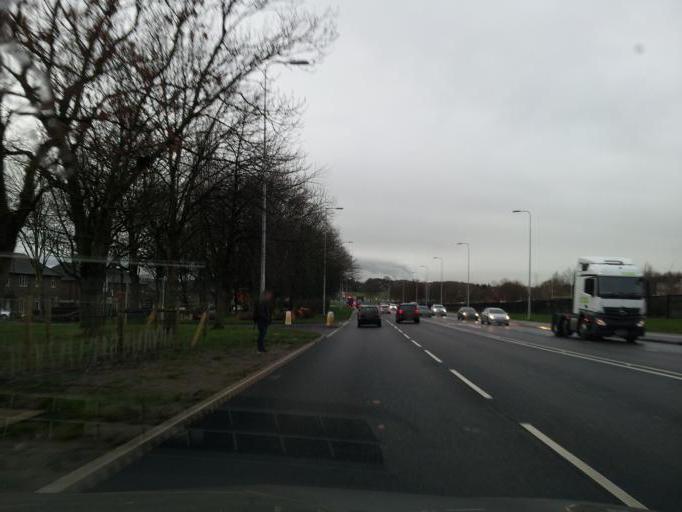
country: GB
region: England
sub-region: Nottinghamshire
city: Ruddington
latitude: 52.9105
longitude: -1.1827
